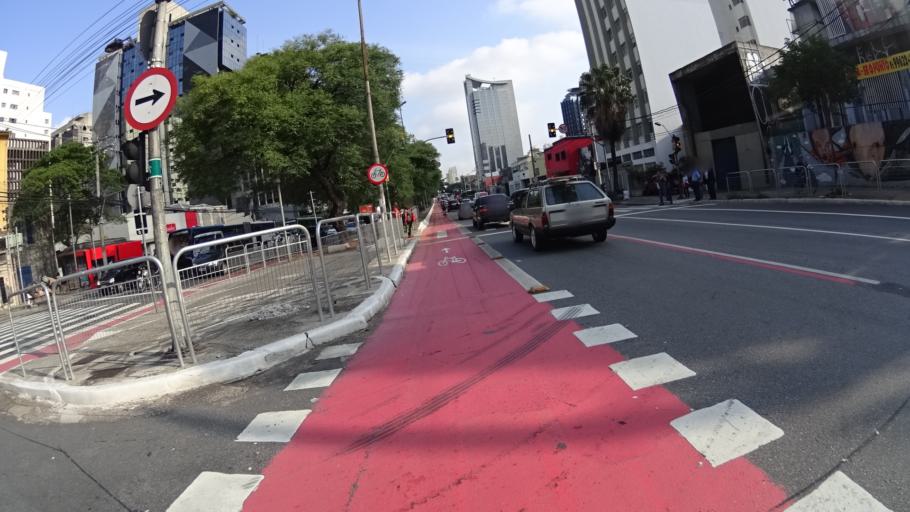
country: BR
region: Sao Paulo
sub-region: Sao Paulo
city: Sao Paulo
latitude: -23.5780
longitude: -46.6406
